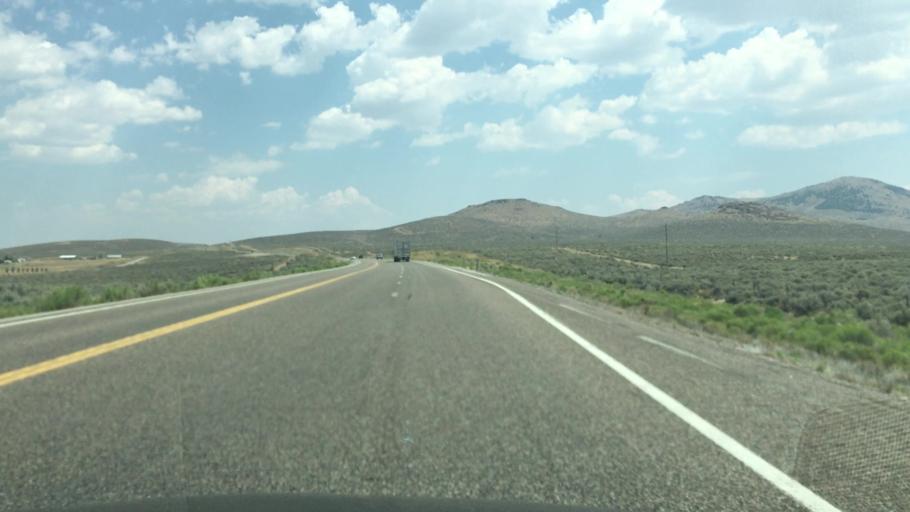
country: US
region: Nevada
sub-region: Elko County
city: Wells
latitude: 41.1707
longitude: -114.8830
